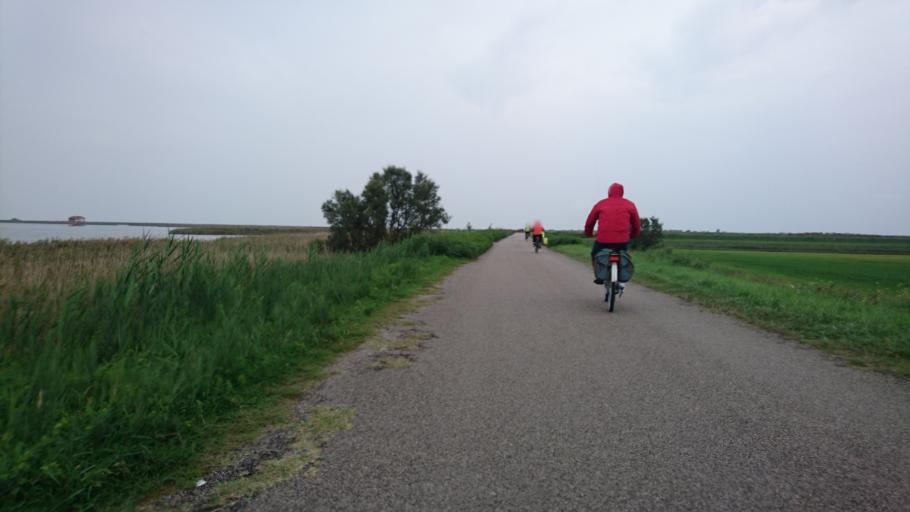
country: IT
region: Veneto
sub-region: Provincia di Rovigo
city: Scardovari
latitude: 44.8171
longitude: 12.4037
